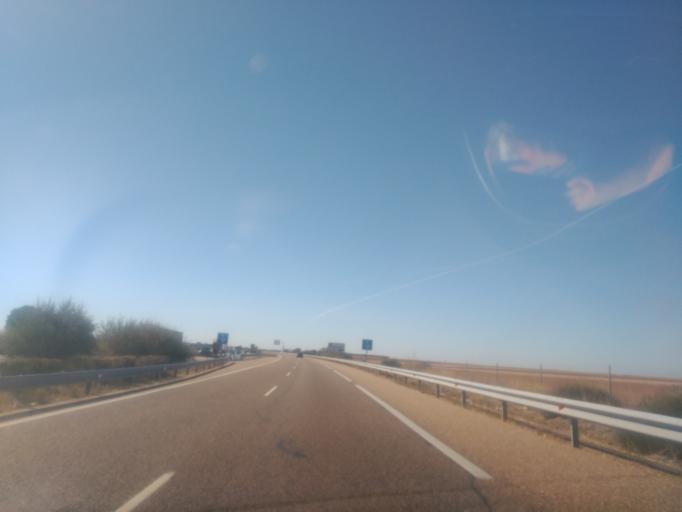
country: ES
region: Castille and Leon
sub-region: Provincia de Salamanca
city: Parada de Rubiales
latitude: 41.1434
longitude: -5.4798
